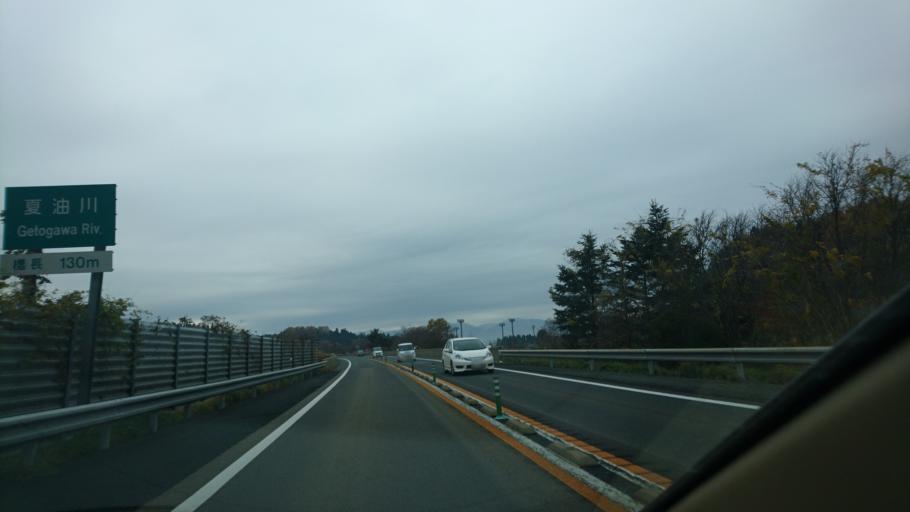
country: JP
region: Iwate
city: Kitakami
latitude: 39.2783
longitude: 141.0452
